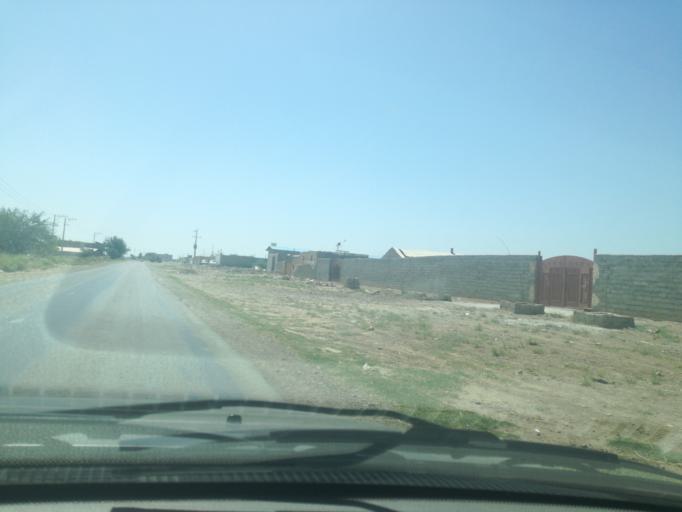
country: IR
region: Razavi Khorasan
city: Sarakhs
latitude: 36.5649
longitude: 61.1436
